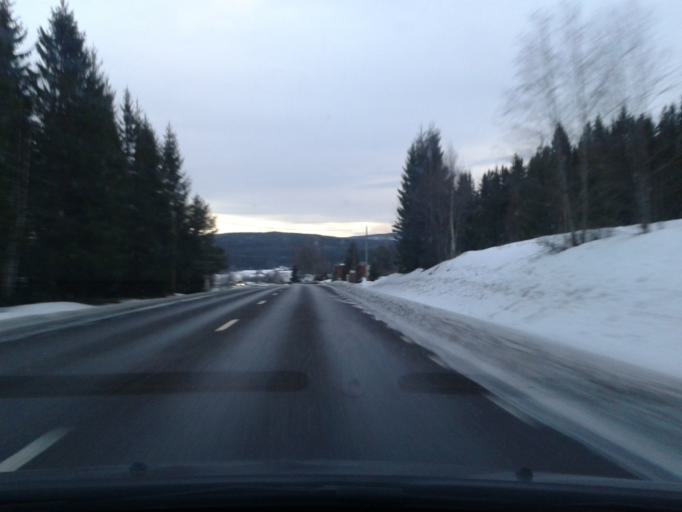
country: SE
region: Vaesternorrland
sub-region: Kramfors Kommun
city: Bollstabruk
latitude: 63.0811
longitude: 17.5384
